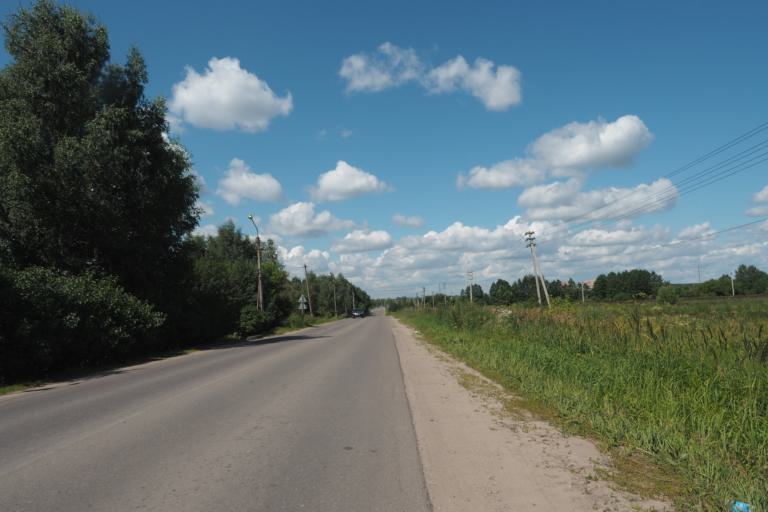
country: RU
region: Moskovskaya
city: Ramenskoye
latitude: 55.5772
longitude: 38.2833
